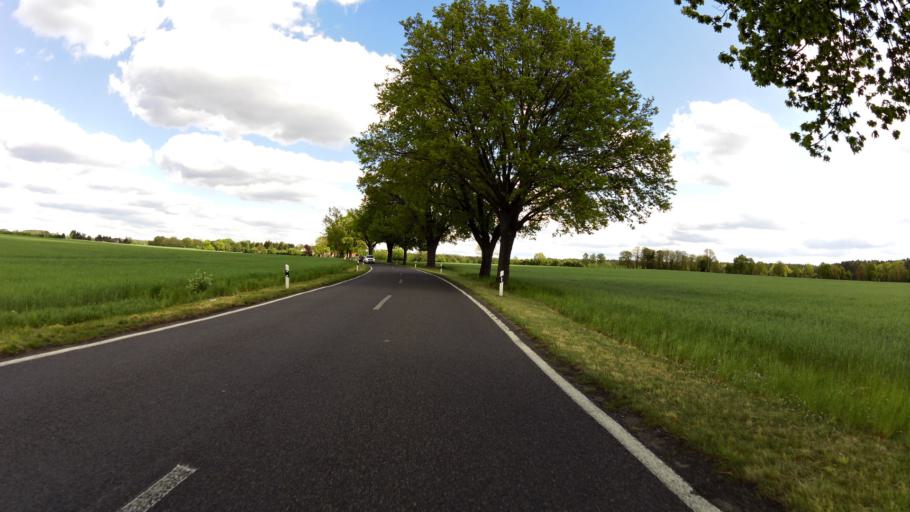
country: DE
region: Brandenburg
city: Wendisch Rietz
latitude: 52.1686
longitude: 14.0672
